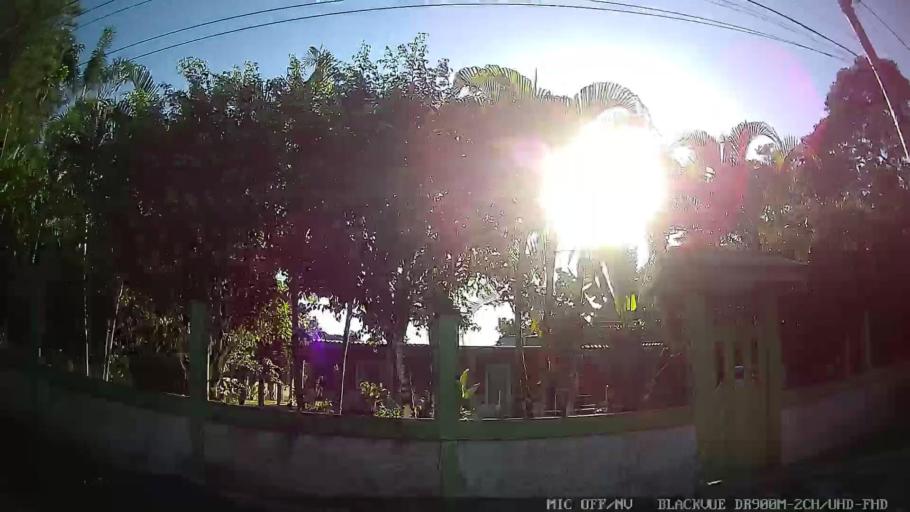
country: BR
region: Sao Paulo
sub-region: Itanhaem
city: Itanhaem
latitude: -24.2028
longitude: -46.8856
